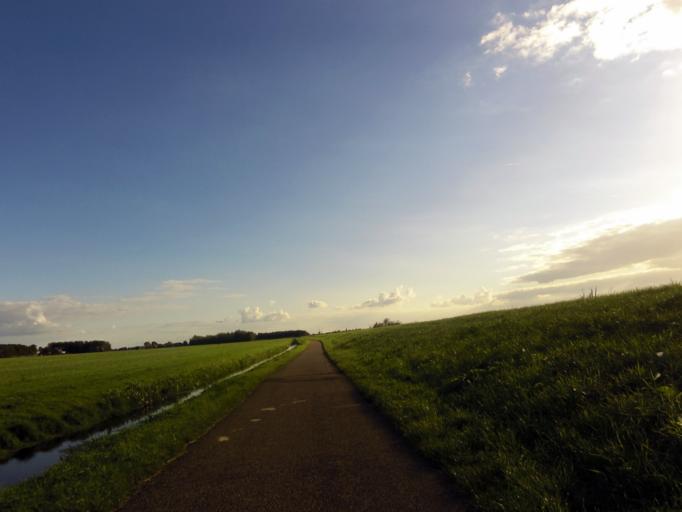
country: NL
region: South Holland
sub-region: Gemeente Alphen aan den Rijn
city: Alphen aan den Rijn
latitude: 52.1234
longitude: 4.6044
